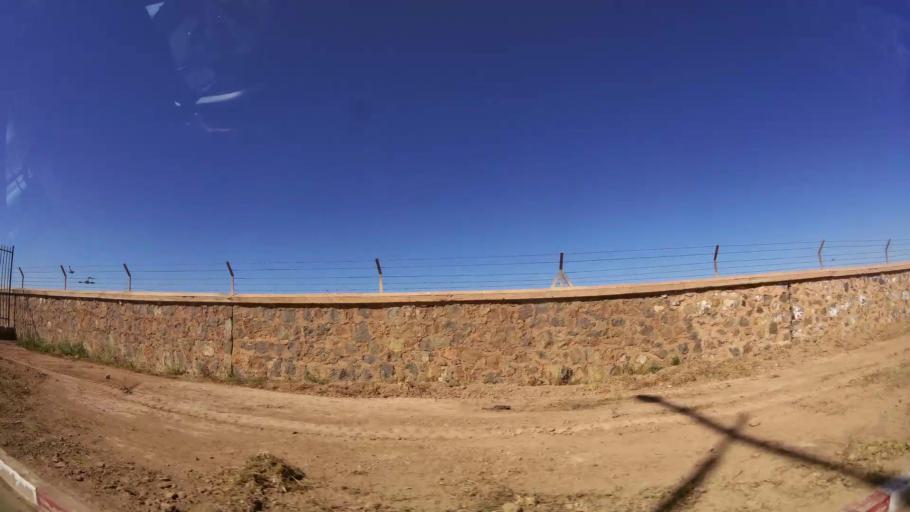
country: MA
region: Oriental
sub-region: Oujda-Angad
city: Oujda
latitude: 34.7765
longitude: -1.9334
